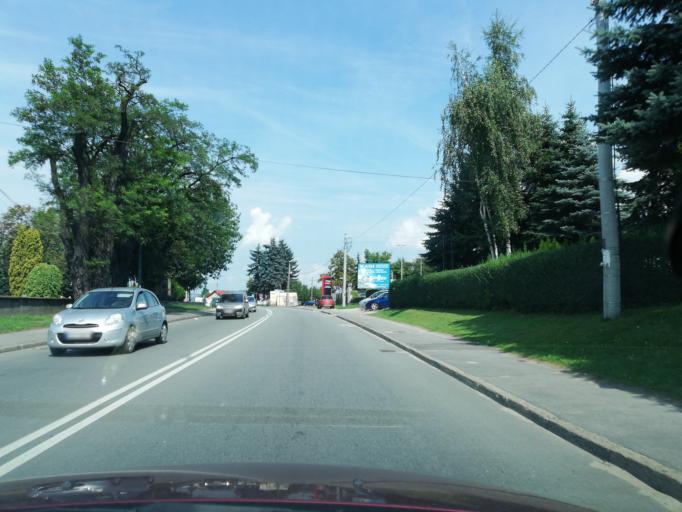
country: PL
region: Lesser Poland Voivodeship
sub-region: Powiat nowosadecki
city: Stary Sacz
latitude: 49.5819
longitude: 20.6706
